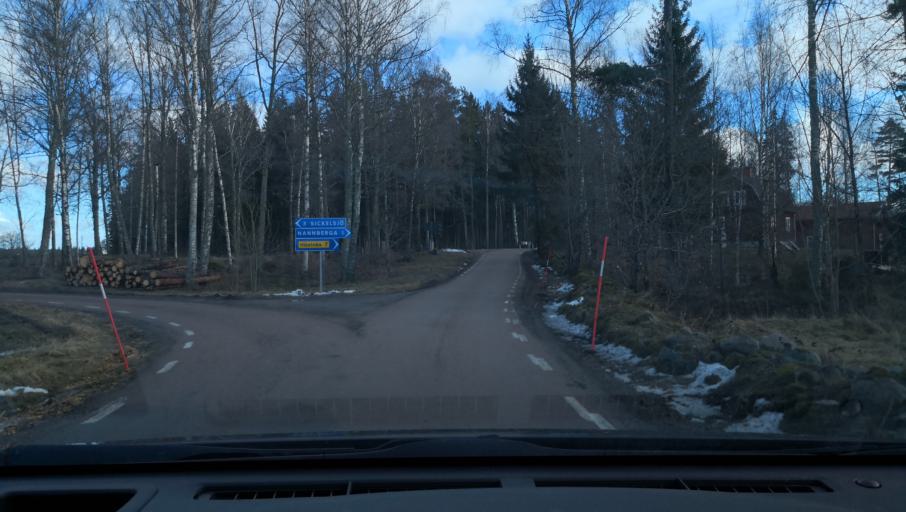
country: SE
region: Vaestmanland
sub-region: Arboga Kommun
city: Arboga
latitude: 59.3162
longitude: 15.7663
